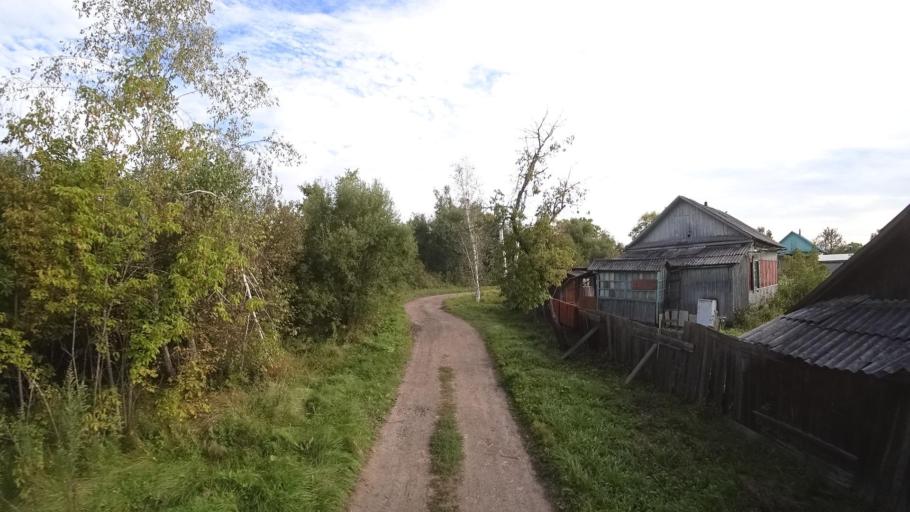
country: RU
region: Primorskiy
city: Dostoyevka
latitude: 44.2888
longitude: 133.4307
